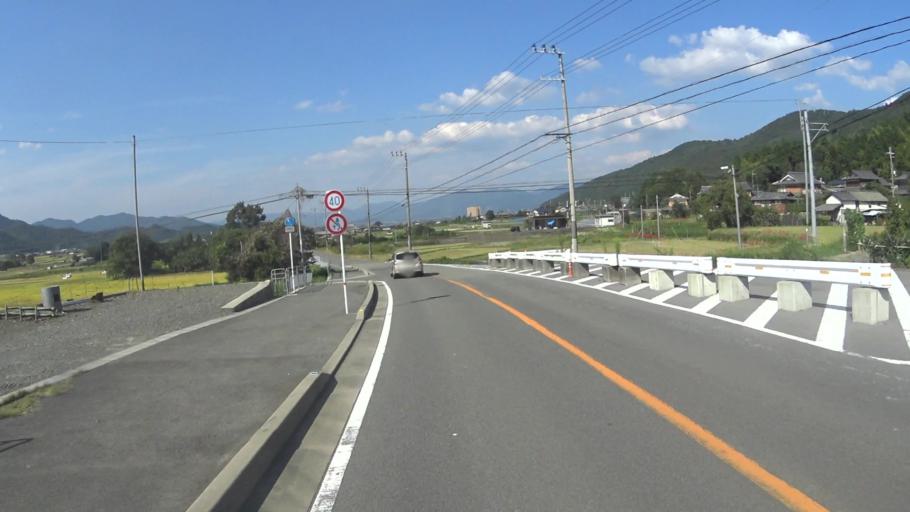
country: JP
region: Kyoto
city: Kameoka
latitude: 34.9828
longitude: 135.5467
